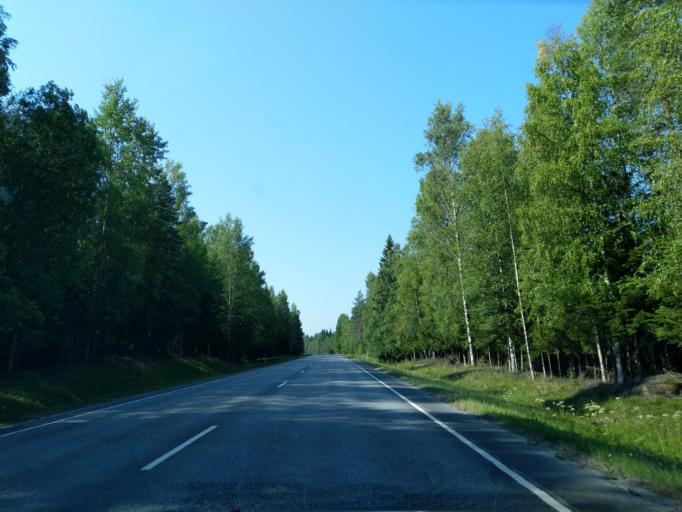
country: FI
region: Satakunta
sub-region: Pori
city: Noormarkku
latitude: 61.6136
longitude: 21.8924
